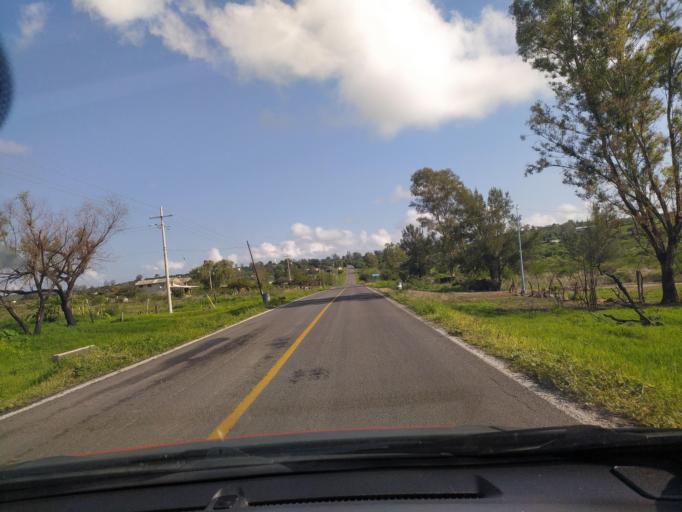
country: MX
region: Guanajuato
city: Ciudad Manuel Doblado
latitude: 20.8224
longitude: -102.0002
